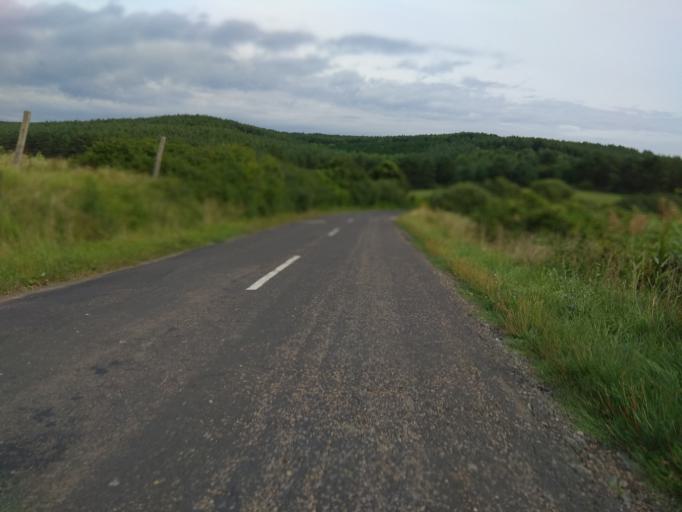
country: HU
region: Heves
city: Tarnalelesz
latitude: 48.0408
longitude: 20.2495
